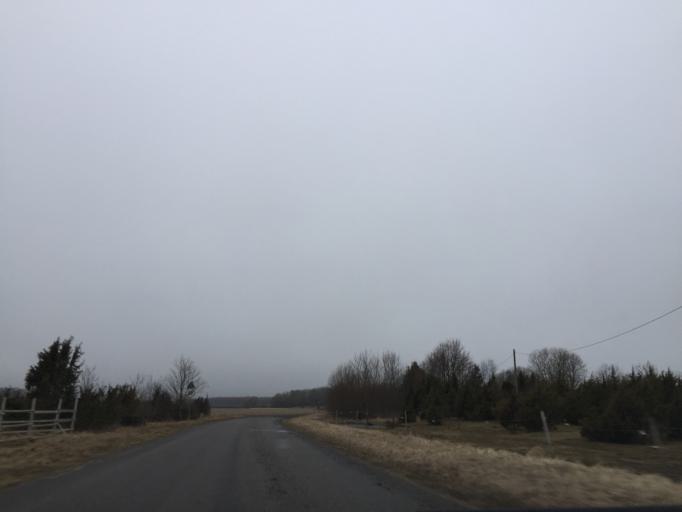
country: EE
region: Laeaene
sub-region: Lihula vald
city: Lihula
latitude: 58.6516
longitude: 23.6148
